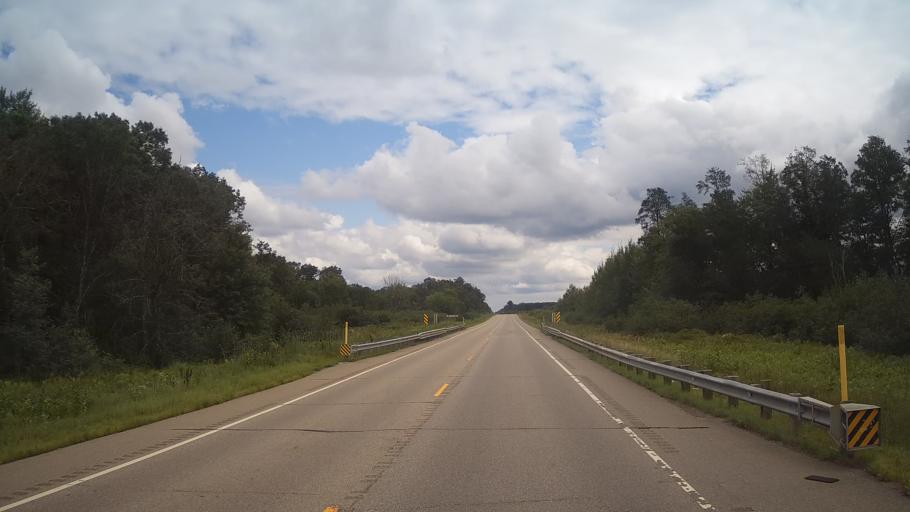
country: US
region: Wisconsin
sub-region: Adams County
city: Friendship
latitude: 44.0250
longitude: -89.7644
